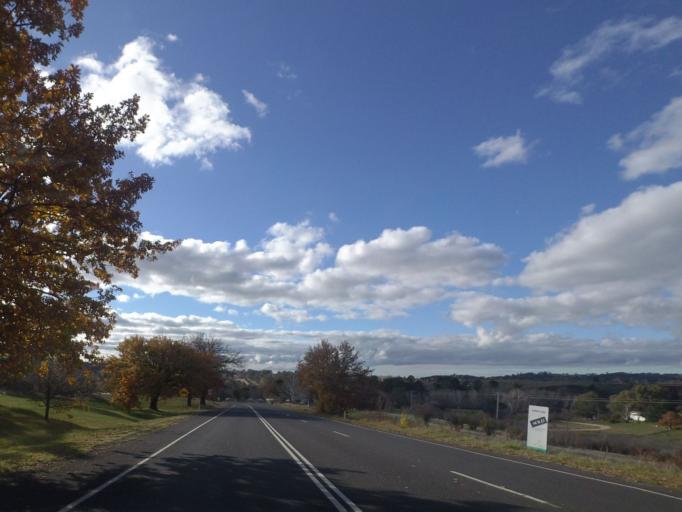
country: AU
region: Victoria
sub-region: Mount Alexander
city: Castlemaine
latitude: -37.1438
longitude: 144.3502
